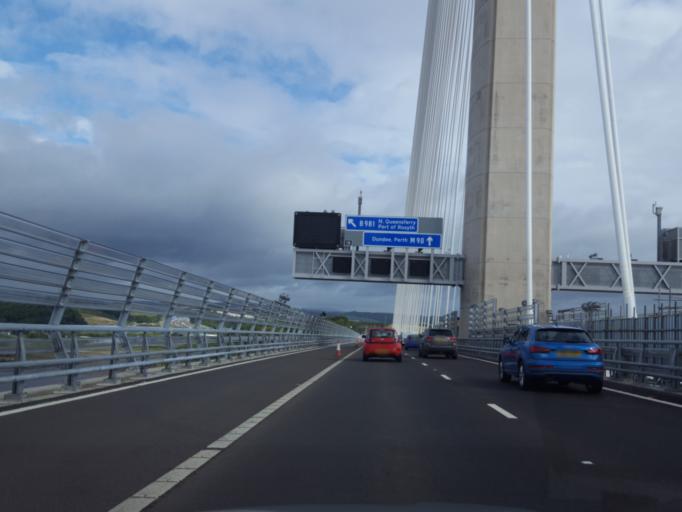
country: GB
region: Scotland
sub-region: Fife
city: North Queensferry
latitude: 56.0096
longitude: -3.4096
